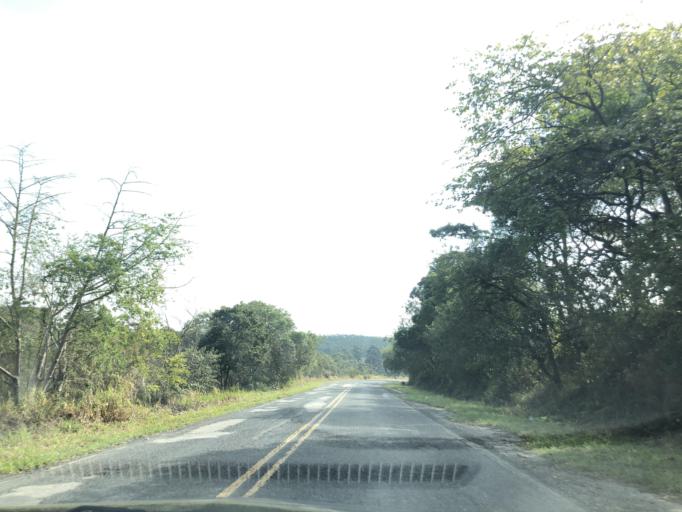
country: BR
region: Sao Paulo
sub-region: Pilar Do Sul
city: Pilar do Sul
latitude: -23.8145
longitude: -47.6354
